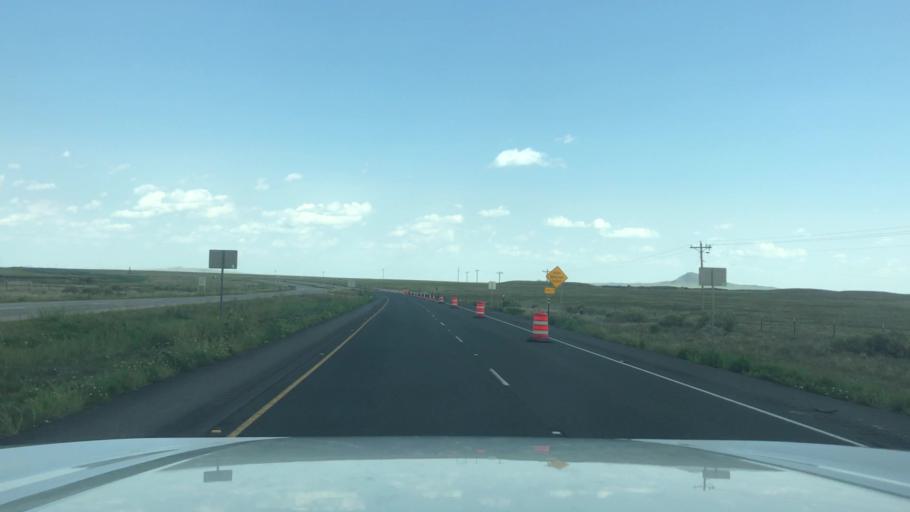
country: US
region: New Mexico
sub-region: Union County
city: Clayton
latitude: 36.6165
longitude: -103.6885
